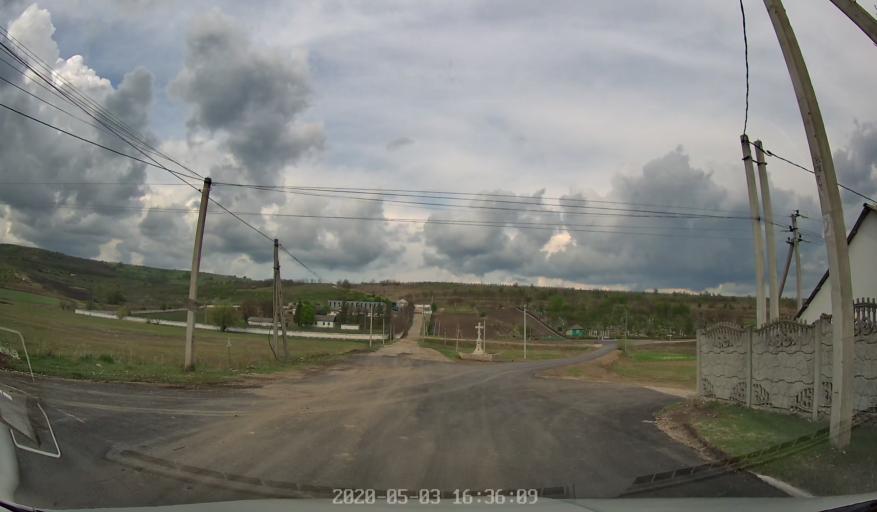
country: MD
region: Calarasi
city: Calarasi
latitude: 47.1933
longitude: 28.3588
